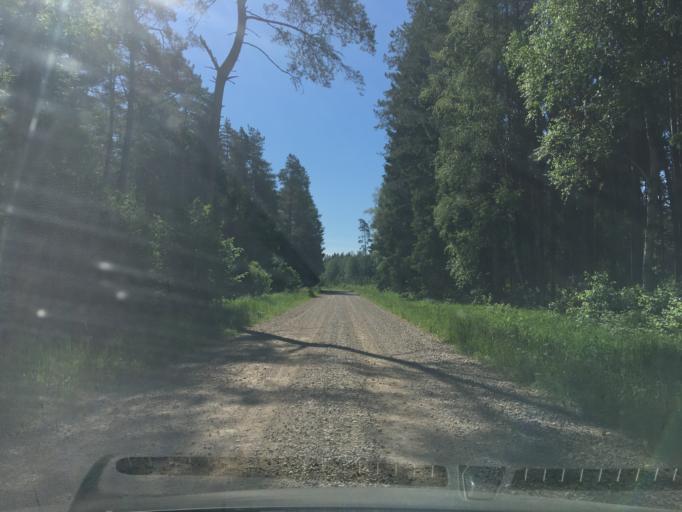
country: EE
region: Laeaene
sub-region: Lihula vald
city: Lihula
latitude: 58.6344
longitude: 23.7993
